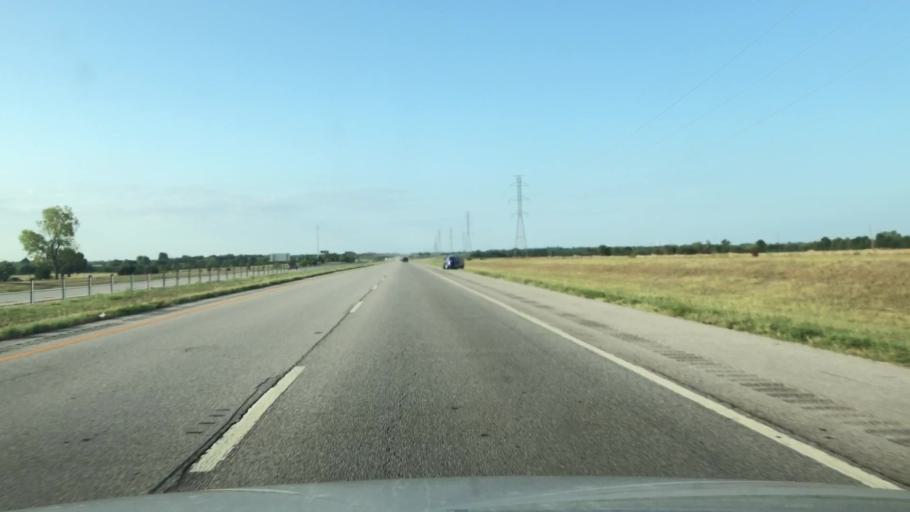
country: US
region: Oklahoma
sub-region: Tulsa County
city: Sperry
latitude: 36.3358
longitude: -95.9241
